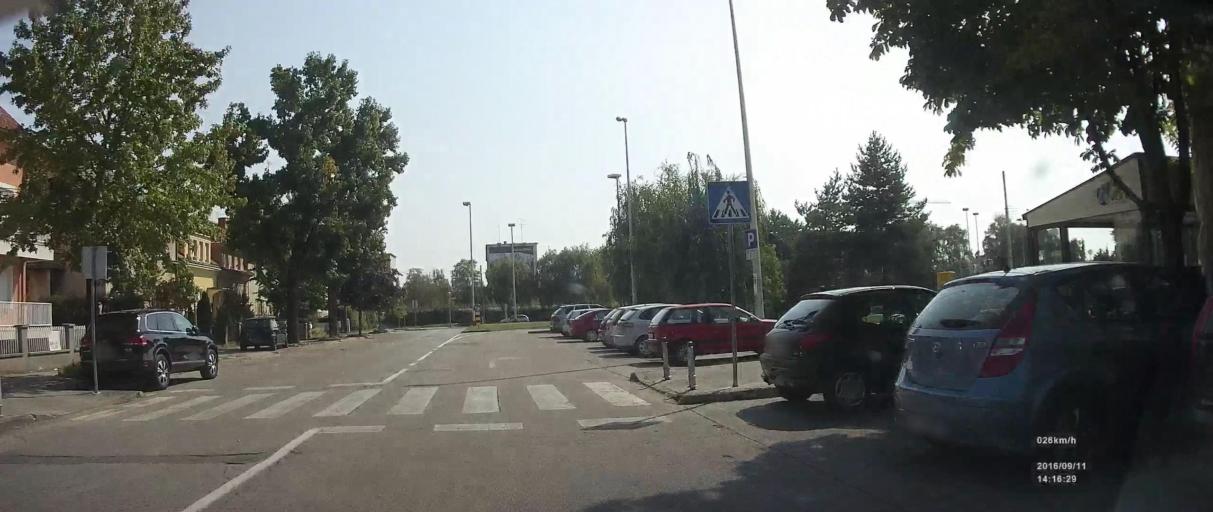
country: HR
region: Grad Zagreb
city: Zagreb
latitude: 45.8145
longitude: 16.0198
